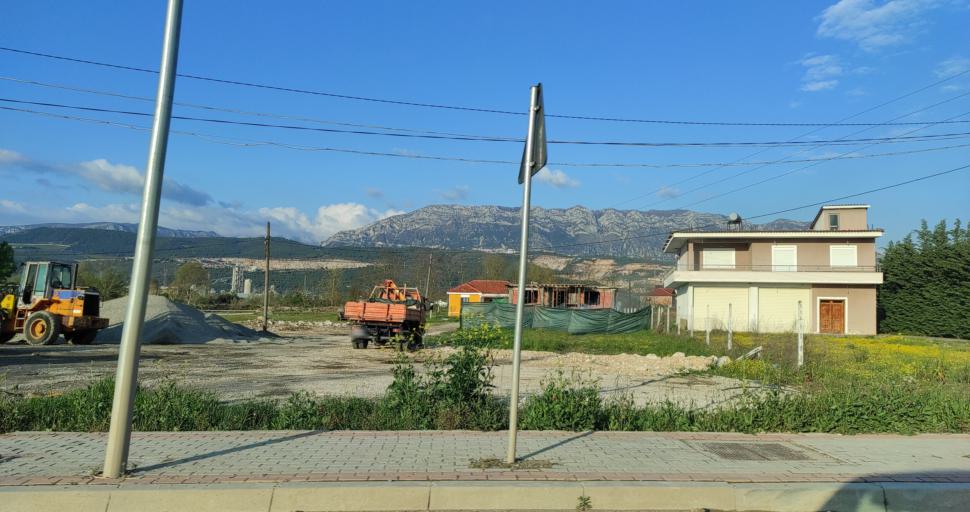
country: AL
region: Durres
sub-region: Rrethi i Krujes
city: Fushe-Kruje
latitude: 41.4881
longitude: 19.7255
